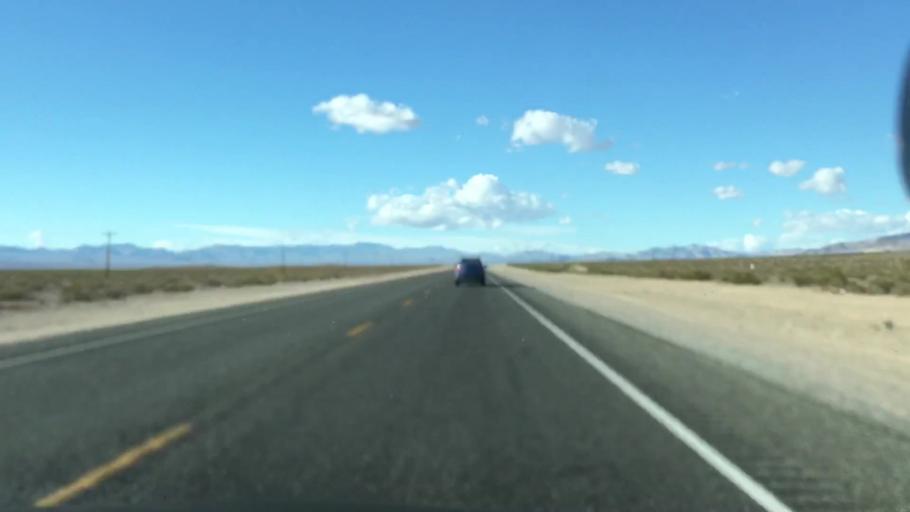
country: US
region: Nevada
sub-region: Nye County
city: Beatty
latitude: 36.7243
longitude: -116.6223
